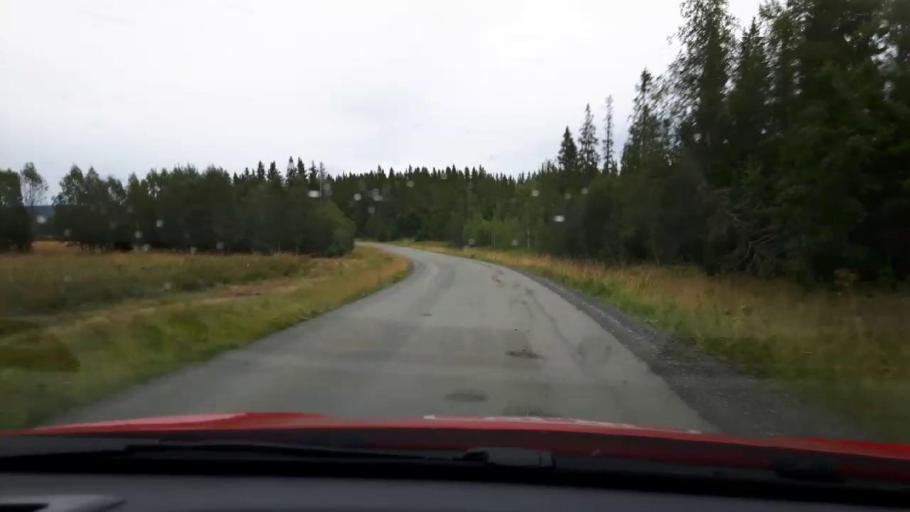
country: SE
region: Jaemtland
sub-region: Are Kommun
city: Jarpen
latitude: 63.4304
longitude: 13.2937
